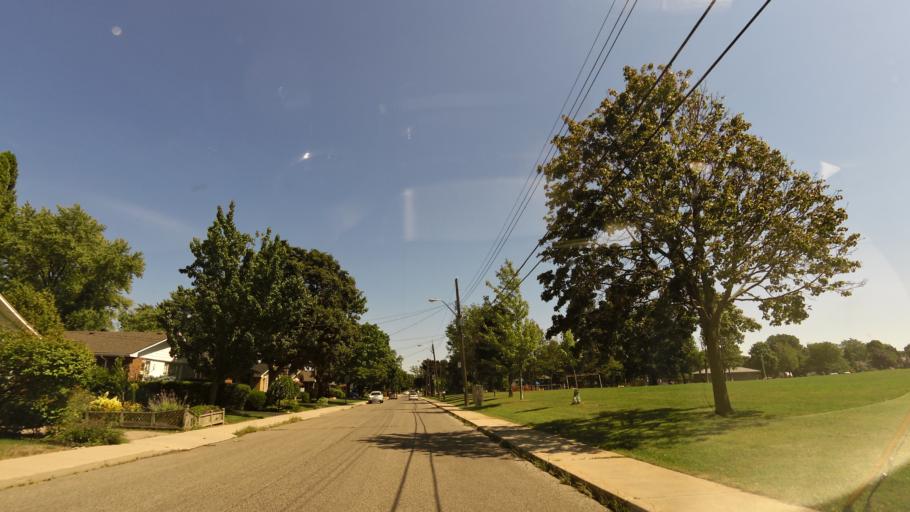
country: CA
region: Ontario
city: Hamilton
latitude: 43.2401
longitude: -79.9059
